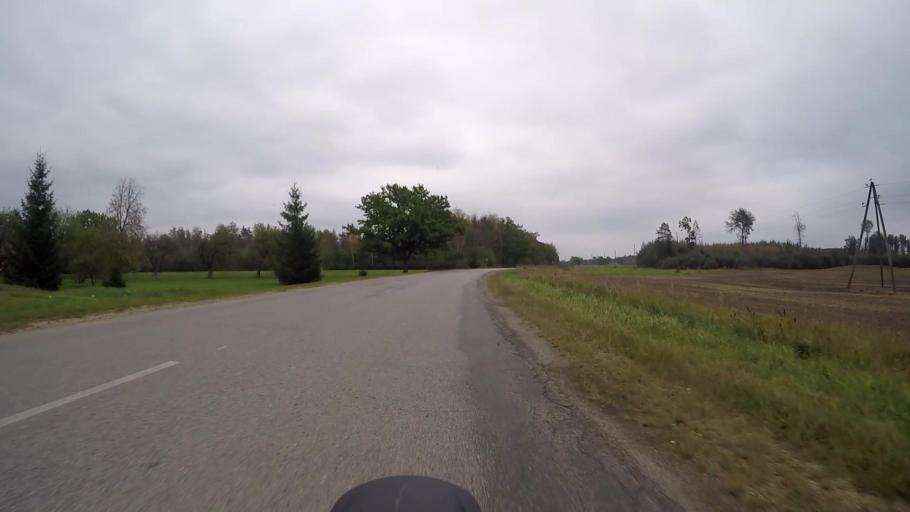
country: LV
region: Saulkrastu
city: Saulkrasti
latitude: 57.2756
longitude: 24.5468
